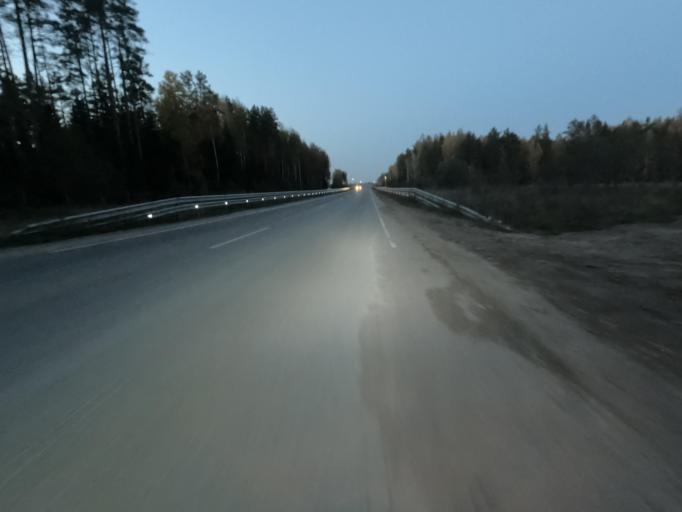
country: RU
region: Leningrad
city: Lyuban'
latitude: 59.1930
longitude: 31.2525
